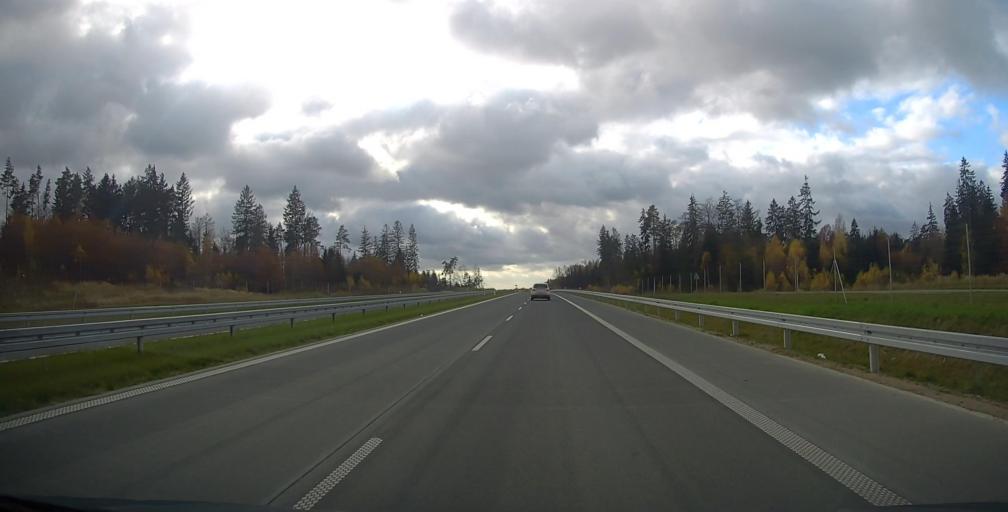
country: PL
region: Podlasie
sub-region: Powiat suwalski
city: Raczki
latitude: 53.8993
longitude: 22.6919
